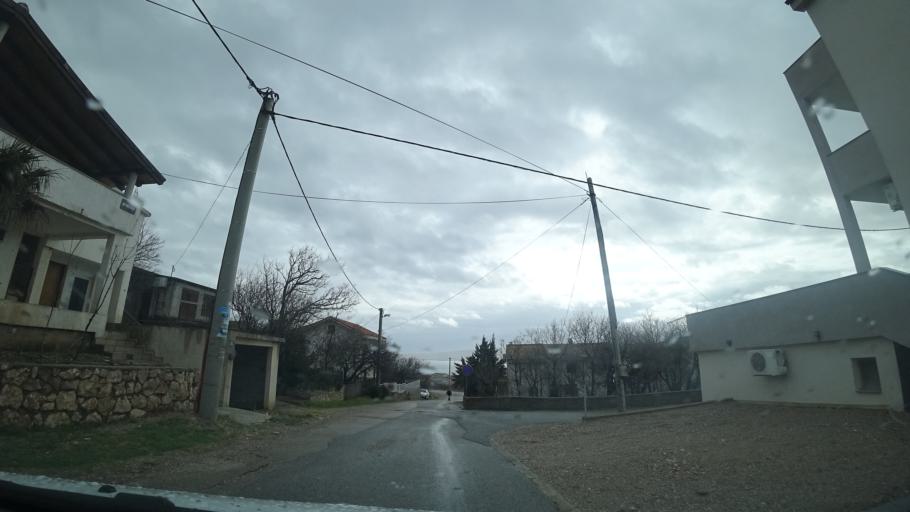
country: HR
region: Licko-Senjska
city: Karlobag
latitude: 44.5311
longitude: 15.0708
